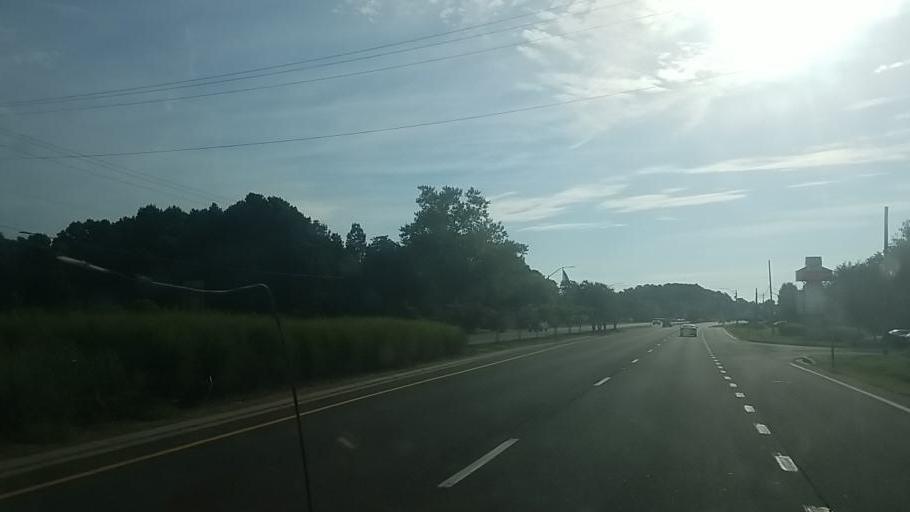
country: US
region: Maryland
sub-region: Worcester County
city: West Ocean City
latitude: 38.3390
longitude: -75.1287
